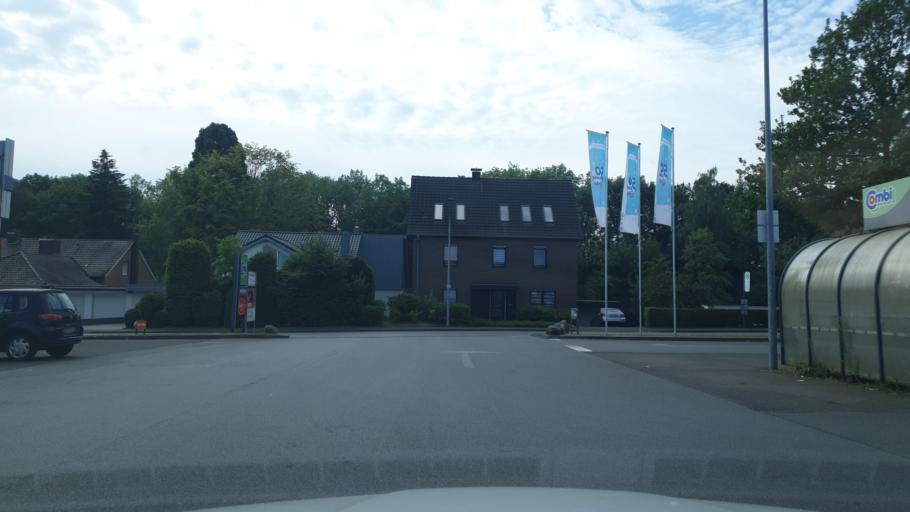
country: DE
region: North Rhine-Westphalia
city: Enger
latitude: 52.0984
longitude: 8.5305
